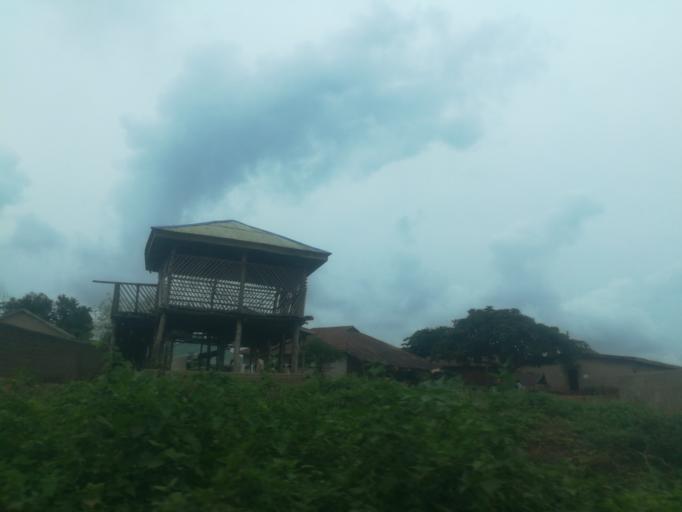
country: NG
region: Ogun
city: Ayetoro
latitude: 7.1121
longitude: 3.1259
